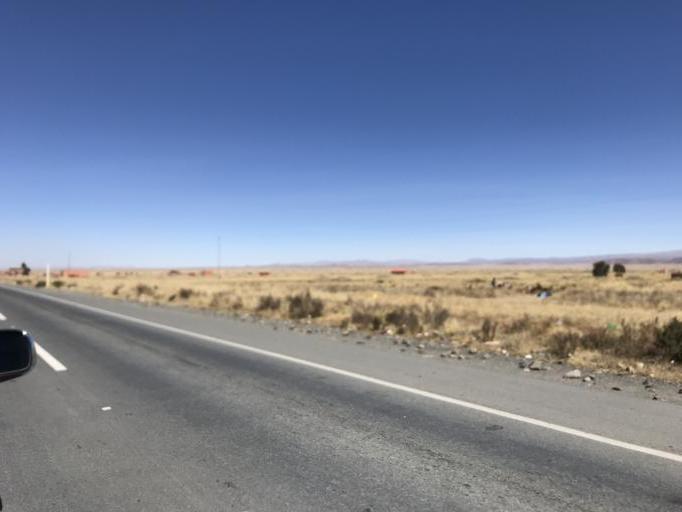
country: BO
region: La Paz
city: Batallas
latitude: -16.3712
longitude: -68.3852
